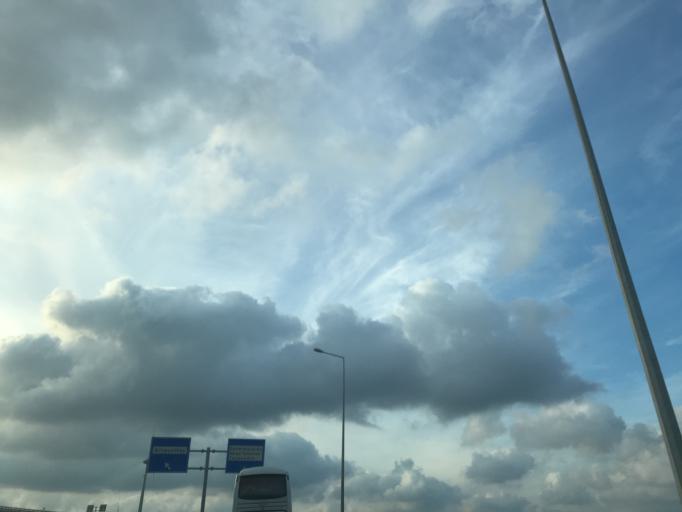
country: TR
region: Istanbul
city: Durusu
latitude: 41.2491
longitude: 28.6989
